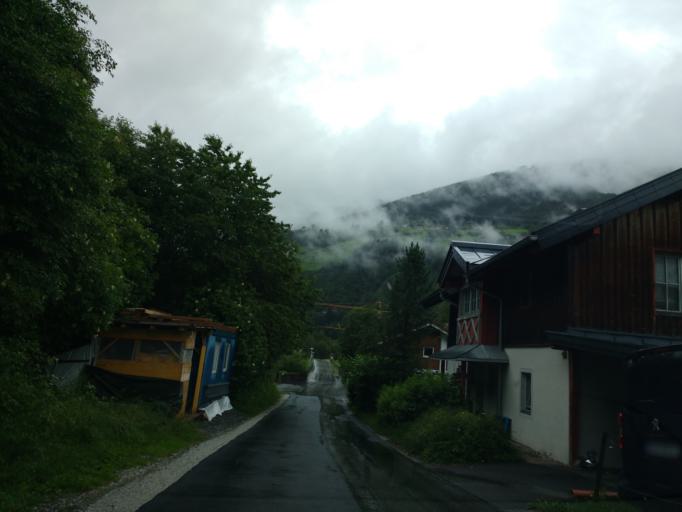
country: AT
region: Salzburg
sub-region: Politischer Bezirk Zell am See
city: Neukirchen am Grossvenediger
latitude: 47.2500
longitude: 12.2859
